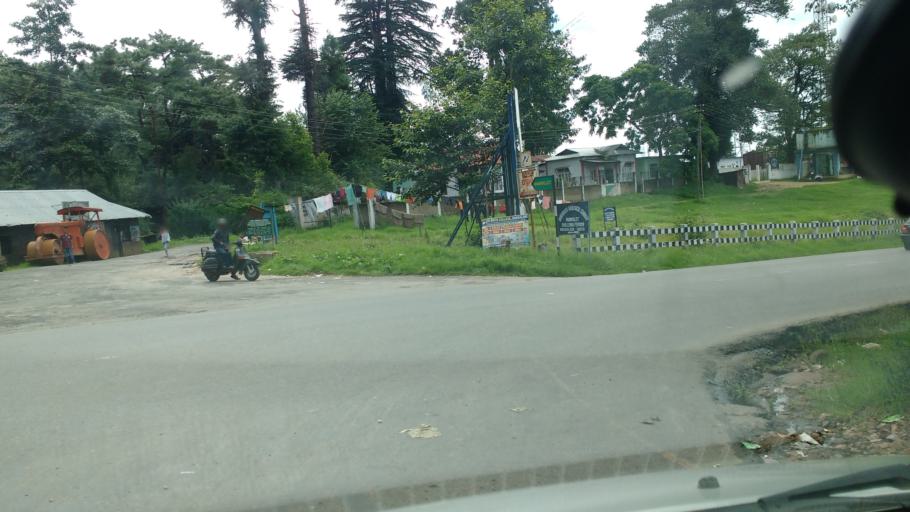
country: IN
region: Meghalaya
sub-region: East Khasi Hills
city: Shillong
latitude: 25.5489
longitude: 91.8419
